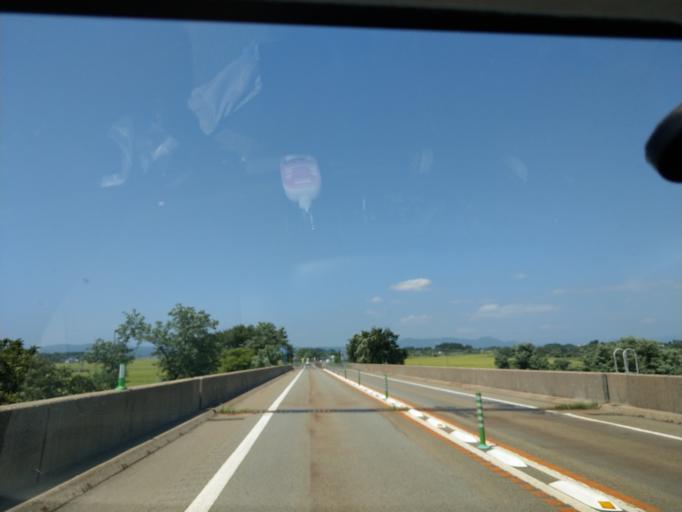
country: JP
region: Akita
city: Yokotemachi
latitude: 39.3330
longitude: 140.5057
